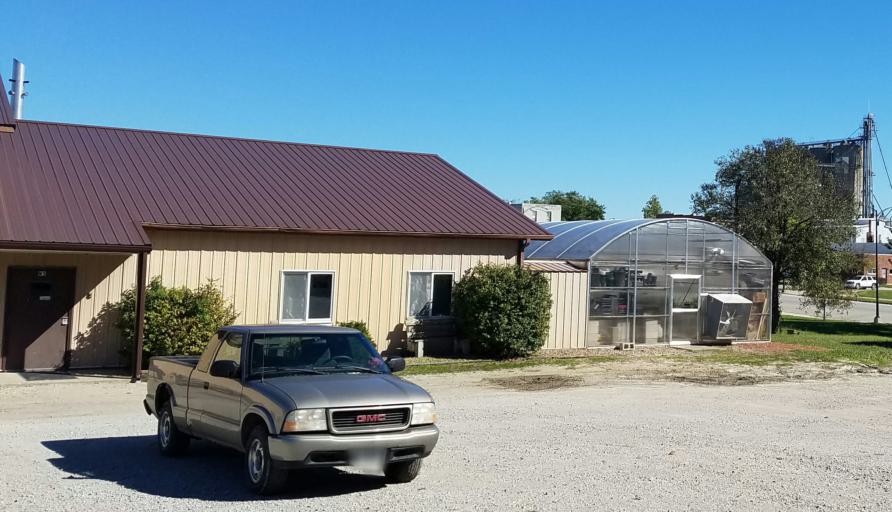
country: US
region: Iowa
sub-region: Decatur County
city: Lamoni
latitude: 40.6244
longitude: -93.9355
